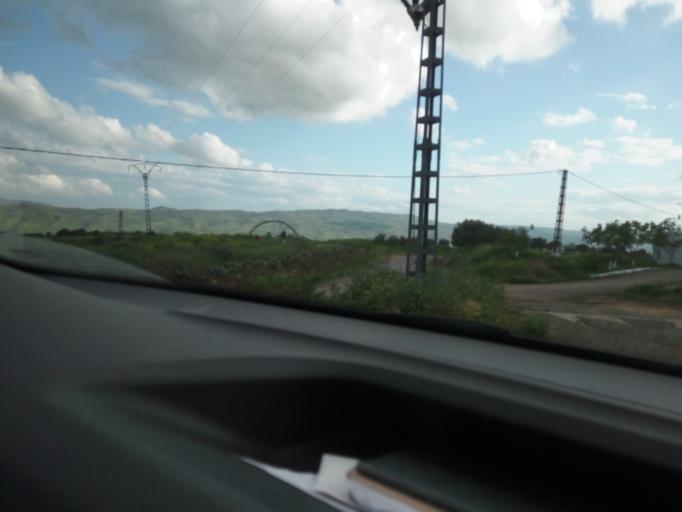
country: DZ
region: Tipaza
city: El Affroun
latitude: 36.3738
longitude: 2.5159
